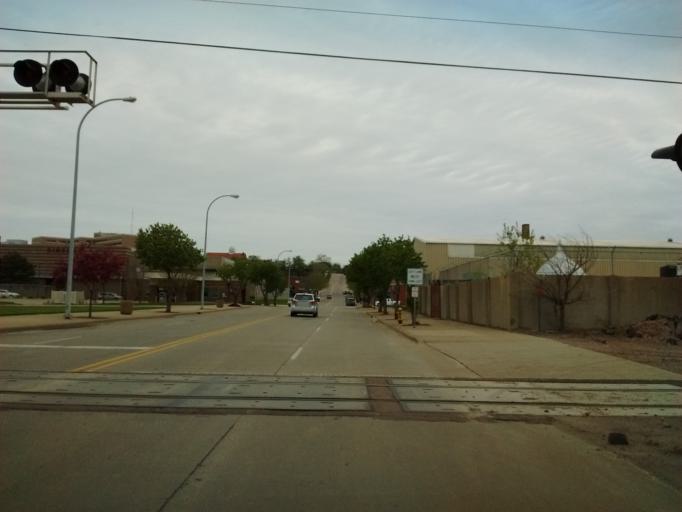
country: US
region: Iowa
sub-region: Woodbury County
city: Sioux City
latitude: 42.4919
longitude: -96.3977
